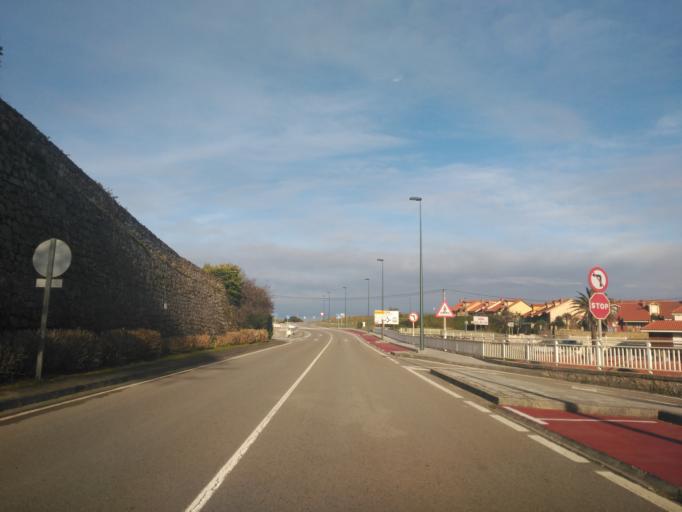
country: ES
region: Cantabria
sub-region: Provincia de Cantabria
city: Comillas
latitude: 43.3900
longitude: -4.2912
